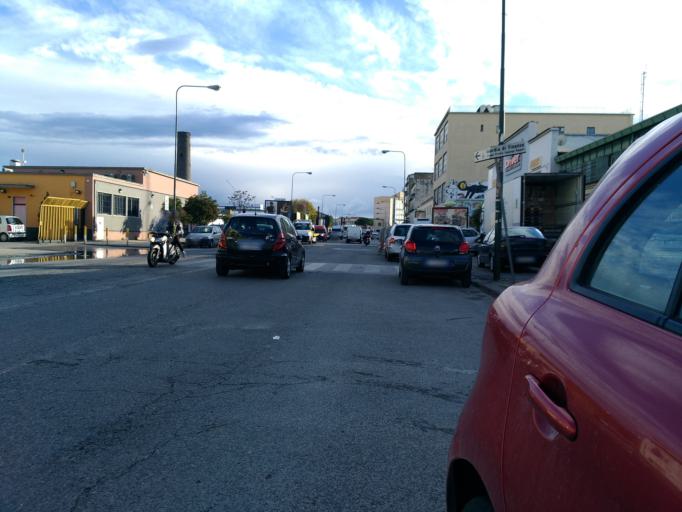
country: IT
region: Campania
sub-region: Provincia di Napoli
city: Napoli
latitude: 40.8521
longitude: 14.2889
